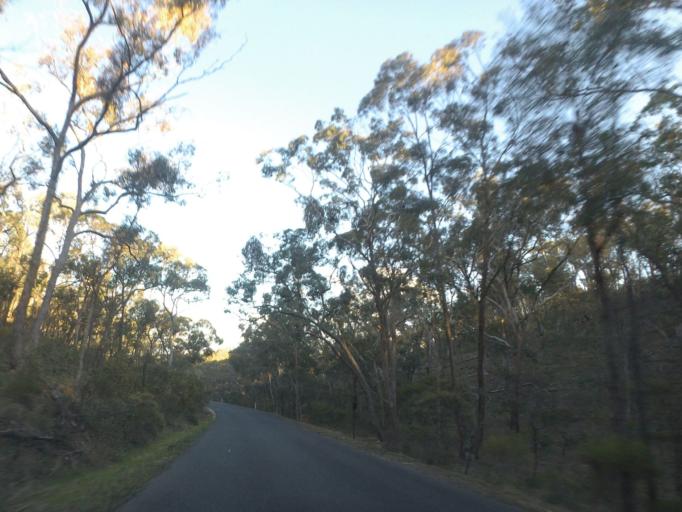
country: AU
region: Victoria
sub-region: Mount Alexander
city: Castlemaine
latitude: -37.1461
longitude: 144.2034
